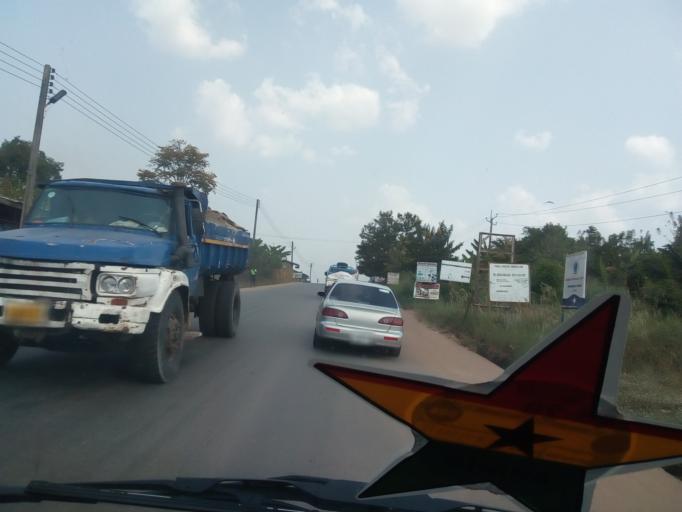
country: GH
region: Eastern
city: Suhum
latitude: 6.0412
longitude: -0.4446
